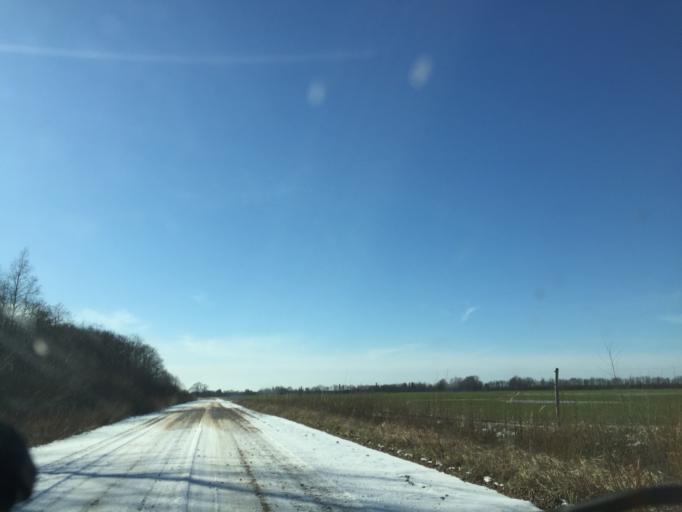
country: LV
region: Ventspils Rajons
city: Piltene
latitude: 57.2700
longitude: 21.6918
